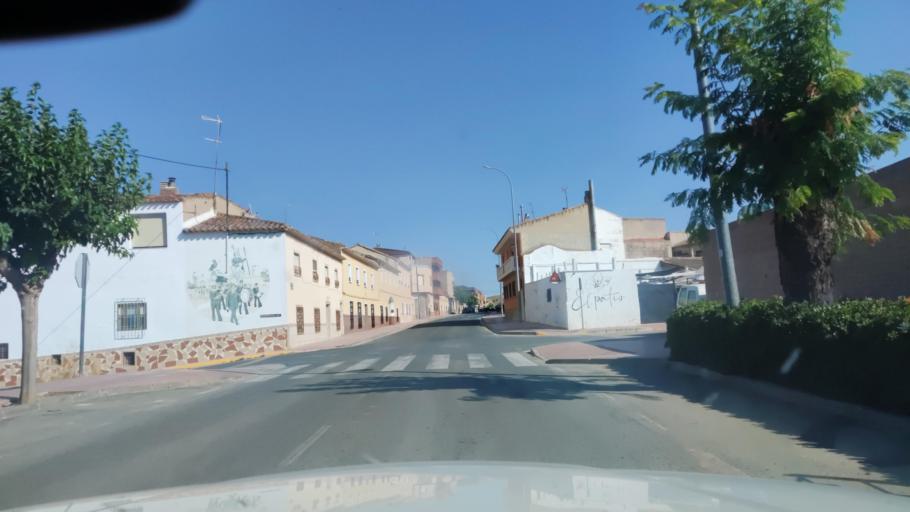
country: ES
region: Castille-La Mancha
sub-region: Provincia de Albacete
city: Pozo-Canada
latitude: 38.8059
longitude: -1.7343
